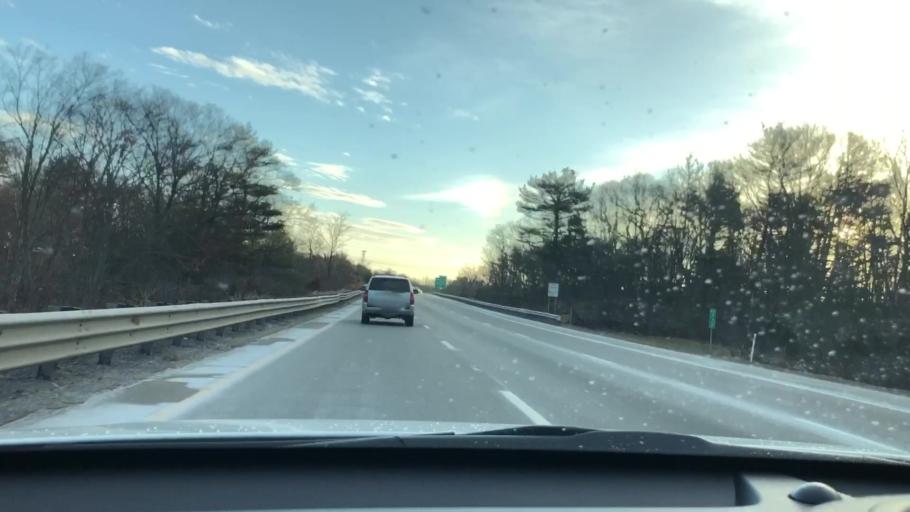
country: US
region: Massachusetts
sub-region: Norfolk County
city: Weymouth
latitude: 42.1878
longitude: -70.9360
